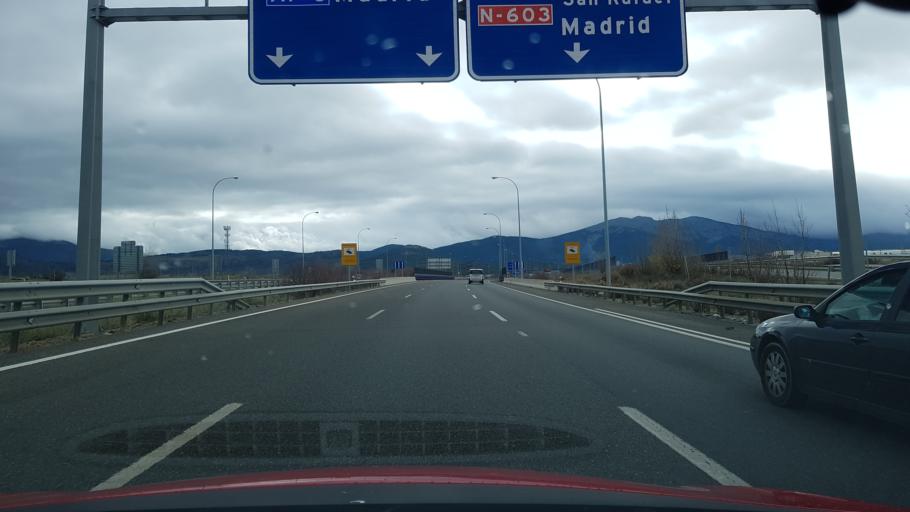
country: ES
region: Castille and Leon
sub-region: Provincia de Segovia
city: Segovia
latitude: 40.9149
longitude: -4.1047
